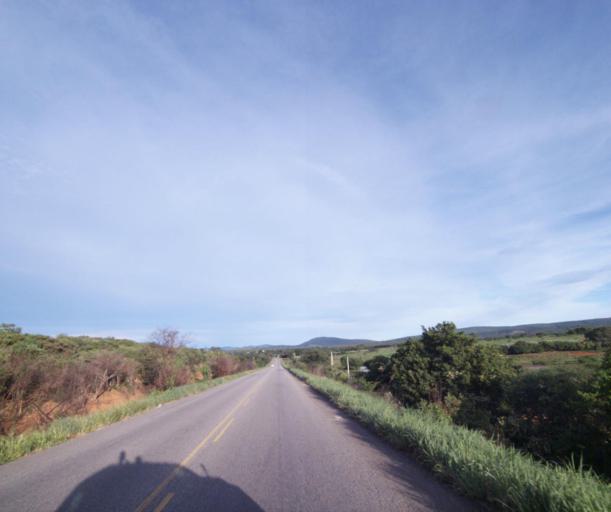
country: BR
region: Bahia
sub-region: Caetite
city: Caetite
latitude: -14.1721
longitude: -42.2006
